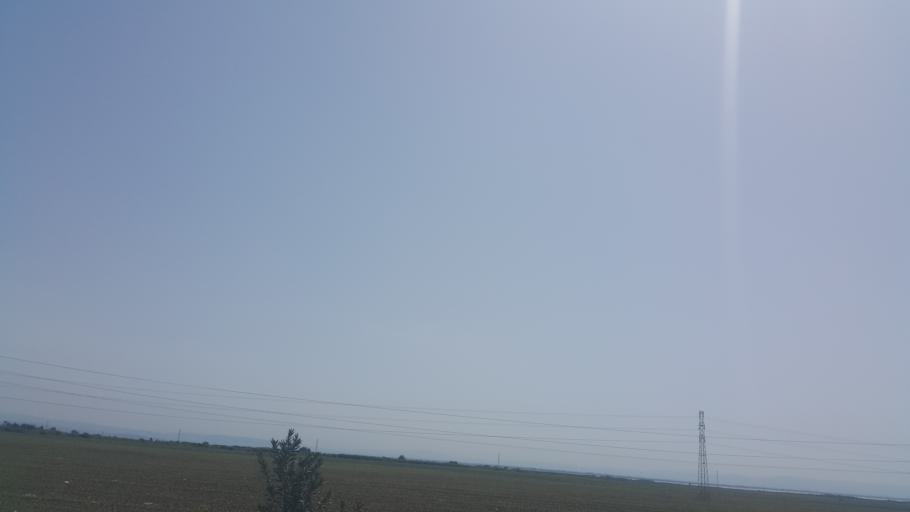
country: TR
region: Hatay
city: Serinyol
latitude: 36.4327
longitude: 36.2799
